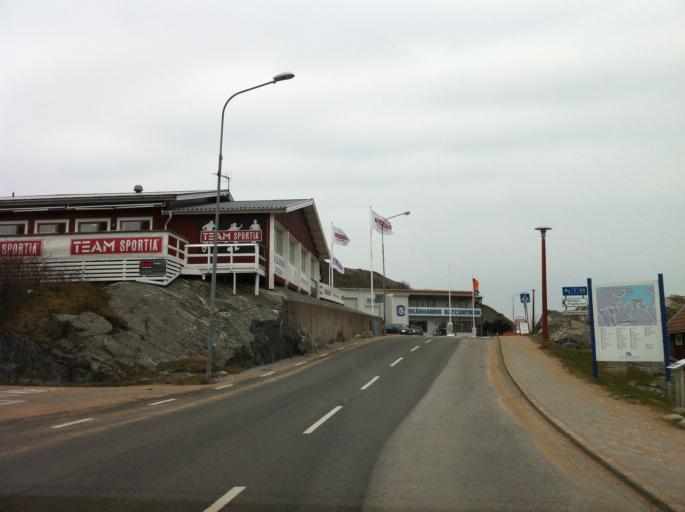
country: SE
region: Vaestra Goetaland
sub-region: Orust
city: Henan
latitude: 58.1525
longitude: 11.7058
